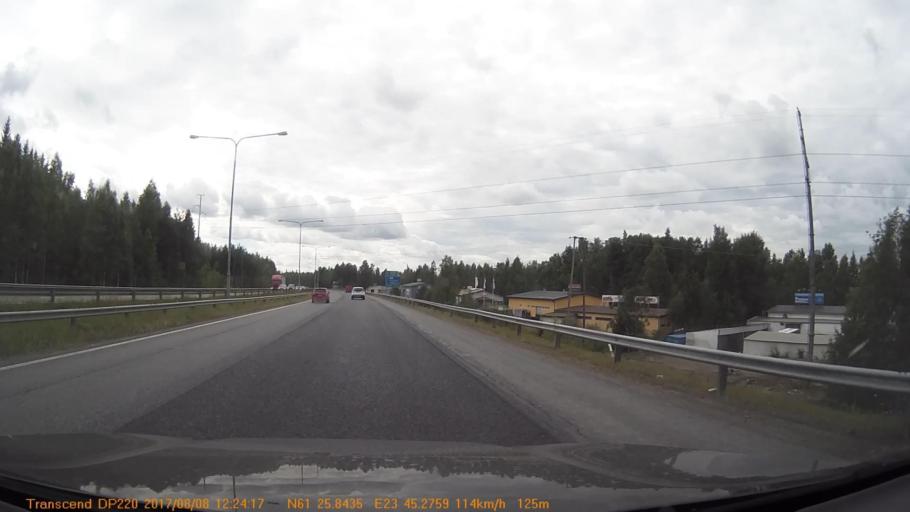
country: FI
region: Pirkanmaa
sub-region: Tampere
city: Tampere
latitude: 61.4304
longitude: 23.7545
